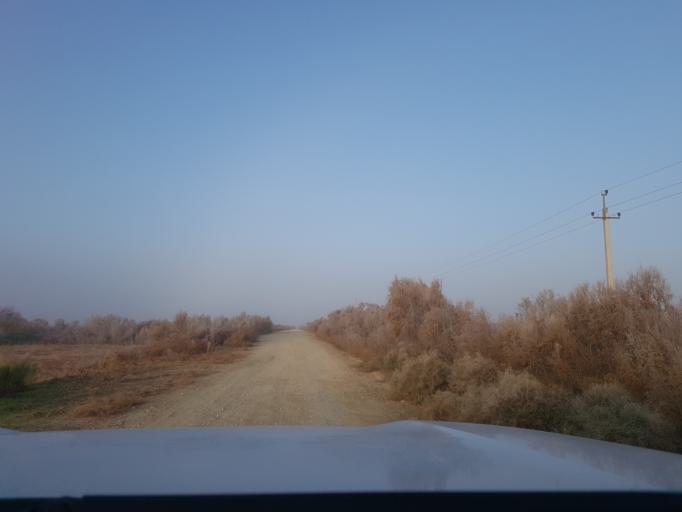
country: TM
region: Dasoguz
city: Koeneuergench
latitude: 41.8486
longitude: 58.3392
